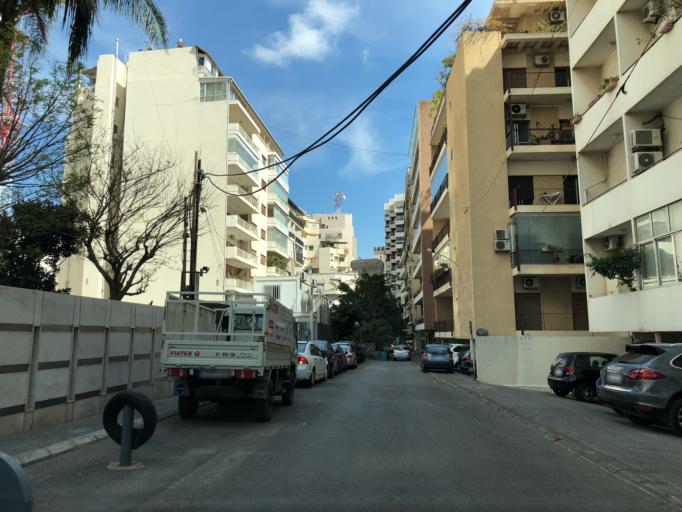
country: LB
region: Beyrouth
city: Beirut
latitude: 33.8873
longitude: 35.5178
